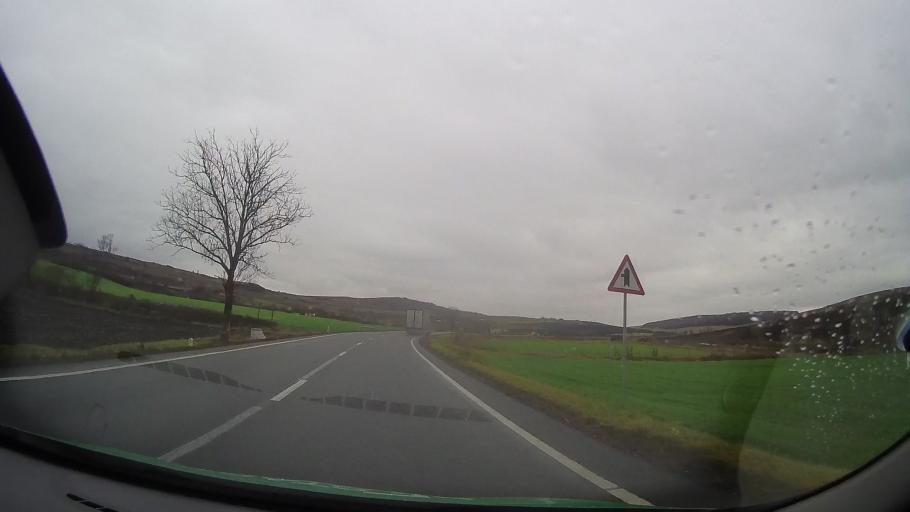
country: RO
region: Mures
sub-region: Comuna Lunca
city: Lunca
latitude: 46.8731
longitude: 24.5485
